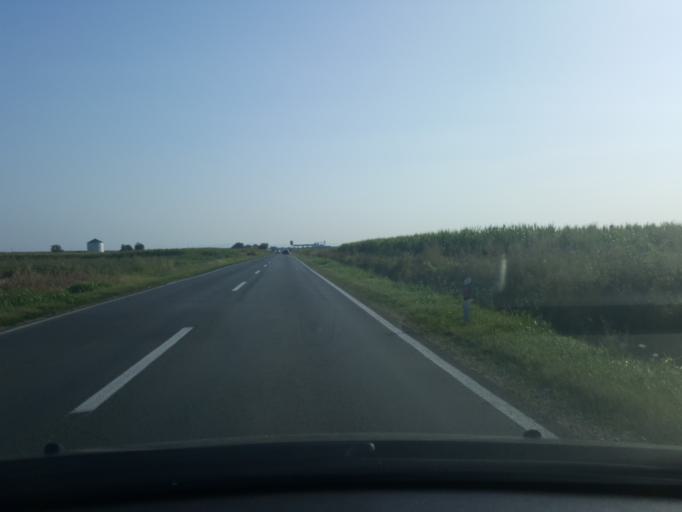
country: RS
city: Jarak
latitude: 44.9371
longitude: 19.7875
